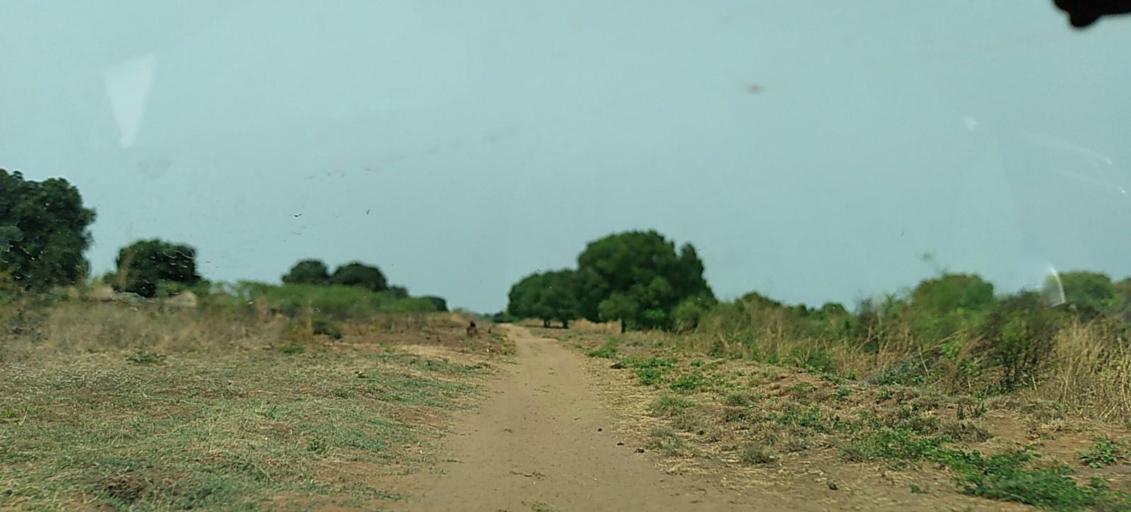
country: ZM
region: Western
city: Lukulu
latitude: -13.9762
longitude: 23.2294
